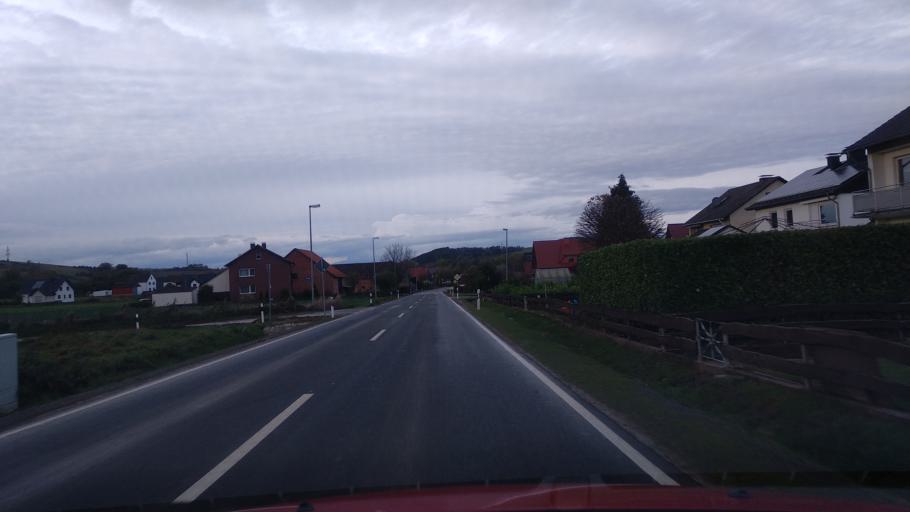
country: DE
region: North Rhine-Westphalia
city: Brakel
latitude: 51.6837
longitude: 9.2265
